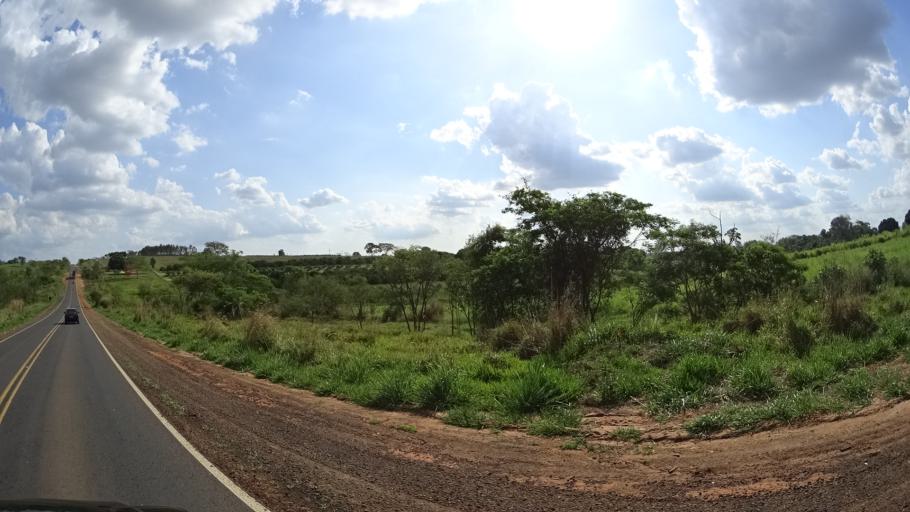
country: BR
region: Sao Paulo
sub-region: Urupes
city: Urupes
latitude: -21.1562
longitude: -49.2850
